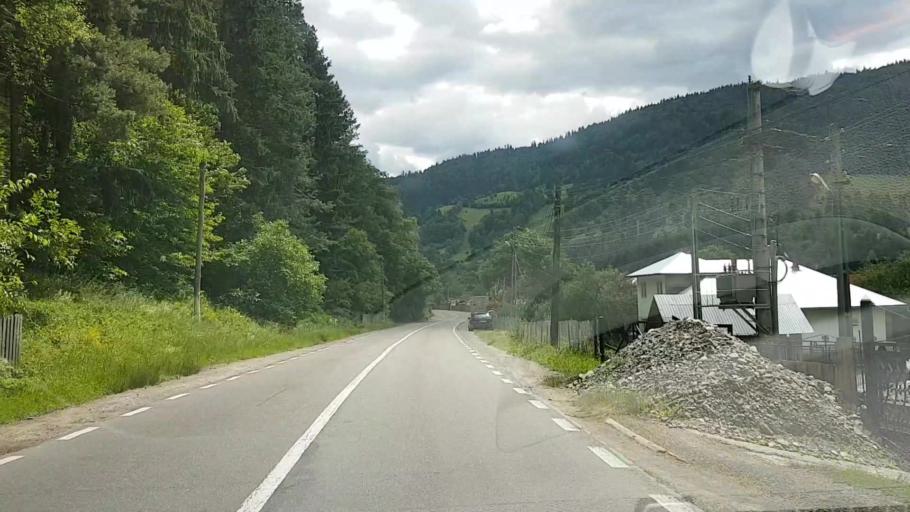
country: RO
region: Neamt
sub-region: Comuna Poiana Teiului
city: Poiana Teiului
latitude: 47.1259
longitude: 25.9067
